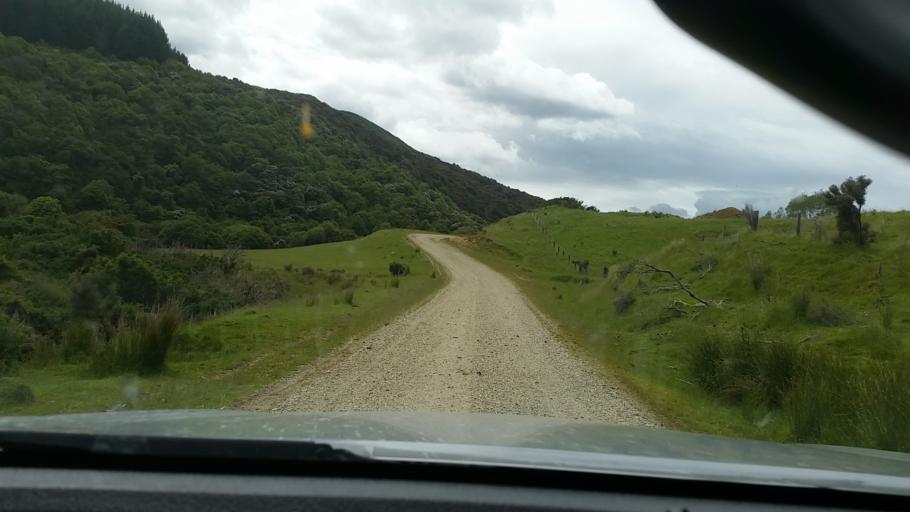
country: NZ
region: Southland
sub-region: Gore District
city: Gore
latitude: -46.3046
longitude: 169.0370
